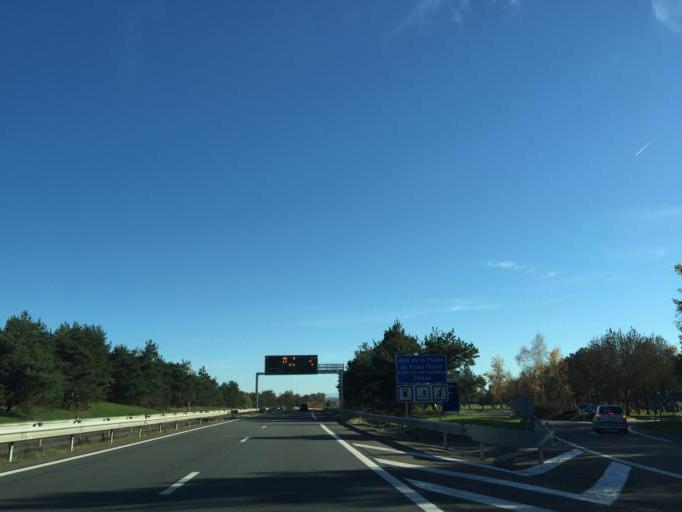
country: FR
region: Rhone-Alpes
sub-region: Departement de la Loire
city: Saint-Germain-Laval
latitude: 45.8412
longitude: 4.0908
